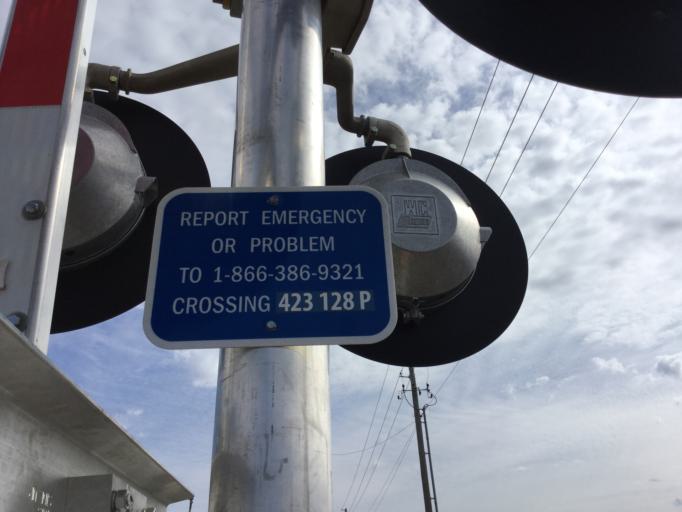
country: US
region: Kansas
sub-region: Crawford County
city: Frontenac
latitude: 37.4330
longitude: -94.6804
